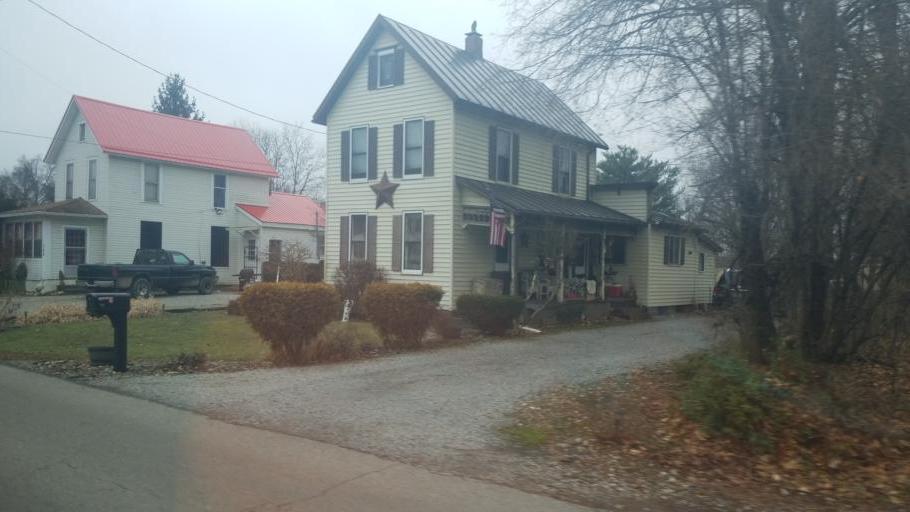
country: US
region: Ohio
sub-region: Crawford County
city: Galion
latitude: 40.7218
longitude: -82.7931
